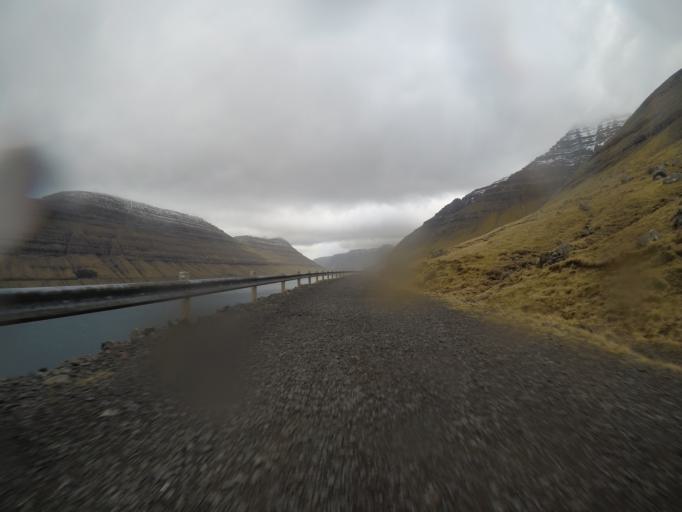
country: FO
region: Nordoyar
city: Klaksvik
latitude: 62.3244
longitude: -6.5624
